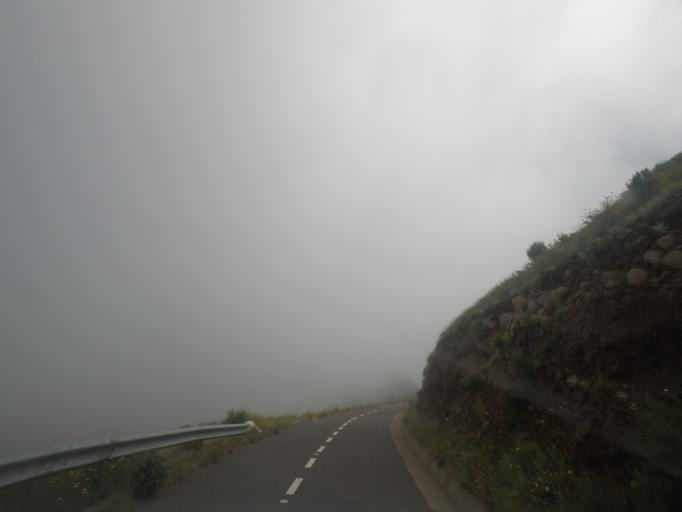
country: PT
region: Madeira
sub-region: Camara de Lobos
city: Curral das Freiras
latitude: 32.7024
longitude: -16.9400
